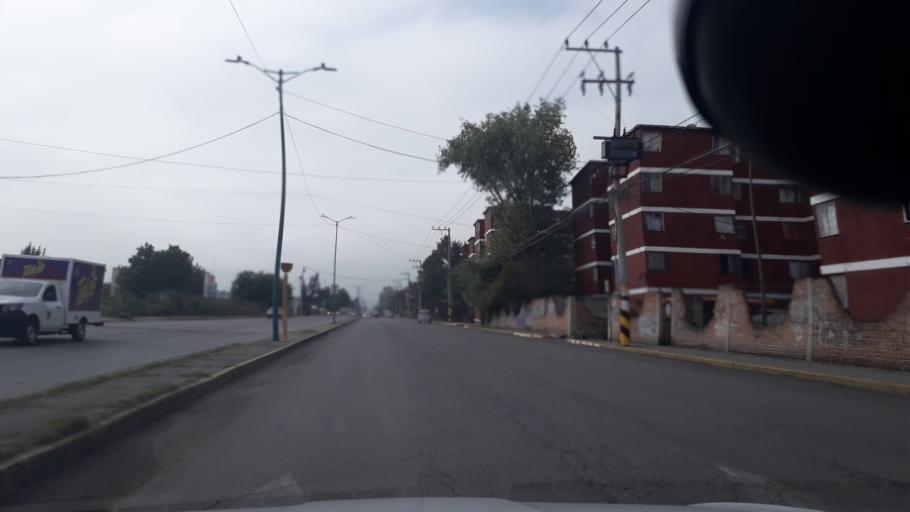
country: MX
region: Mexico
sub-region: Jaltenco
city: Alborada Jaltenco
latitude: 19.6561
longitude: -99.0762
